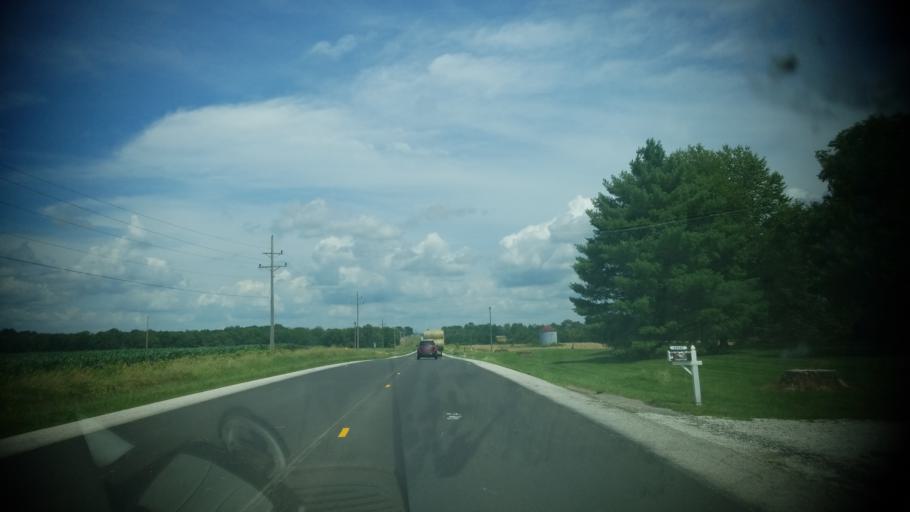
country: US
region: Missouri
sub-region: Pike County
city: Bowling Green
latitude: 39.3444
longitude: -91.2813
